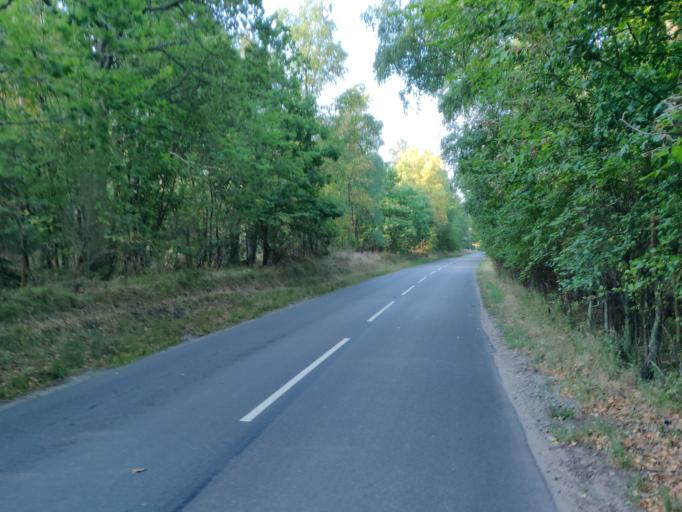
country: DK
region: Zealand
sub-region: Odsherred Kommune
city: Hojby
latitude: 55.8878
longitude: 11.5432
